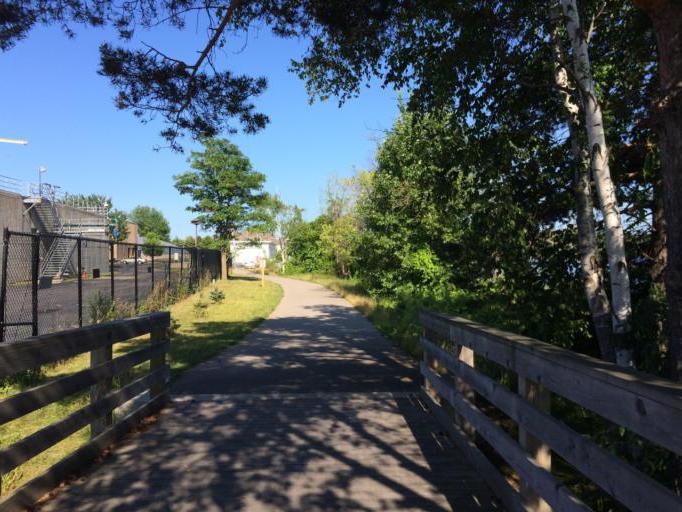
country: US
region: Michigan
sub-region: Grand Traverse County
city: Traverse City
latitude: 44.7571
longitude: -85.6137
